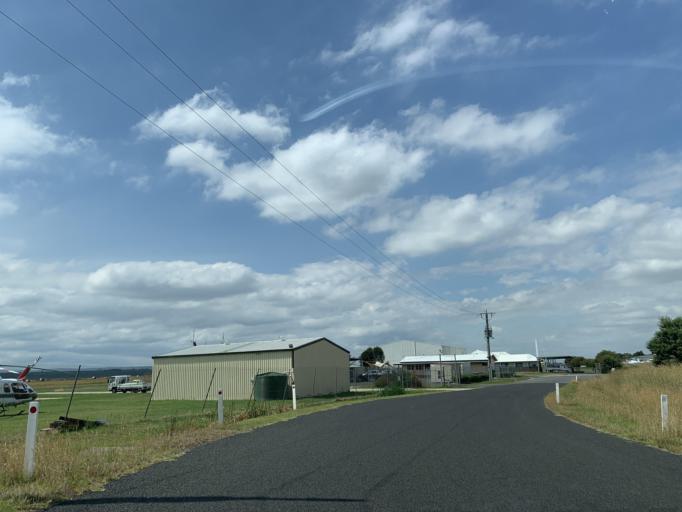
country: AU
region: Victoria
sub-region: Latrobe
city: Traralgon
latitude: -38.2141
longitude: 146.4695
